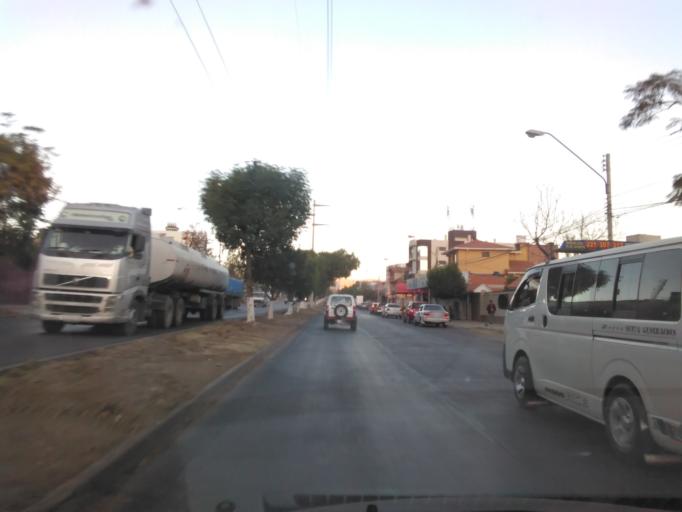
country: BO
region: Cochabamba
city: Cochabamba
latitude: -17.3675
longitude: -66.1485
